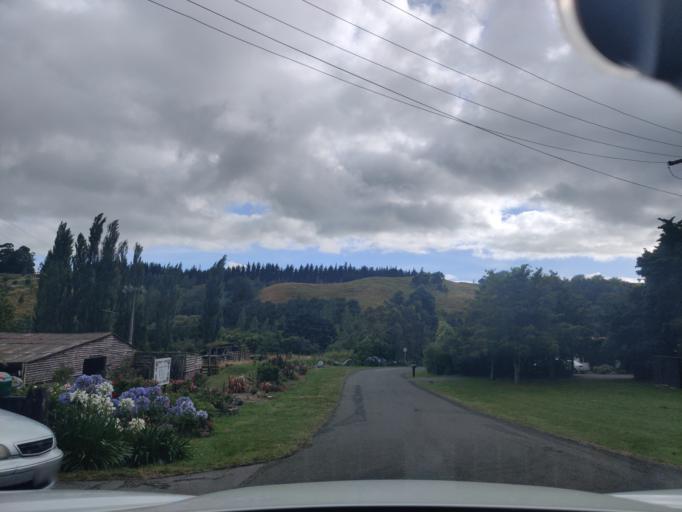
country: NZ
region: Manawatu-Wanganui
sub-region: Palmerston North City
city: Palmerston North
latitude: -40.3766
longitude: 175.6653
